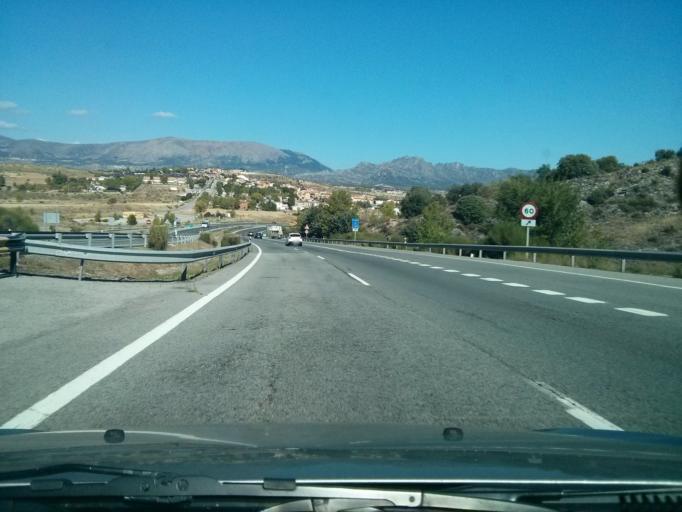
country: ES
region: Madrid
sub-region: Provincia de Madrid
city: Venturada
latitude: 40.7899
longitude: -3.6161
